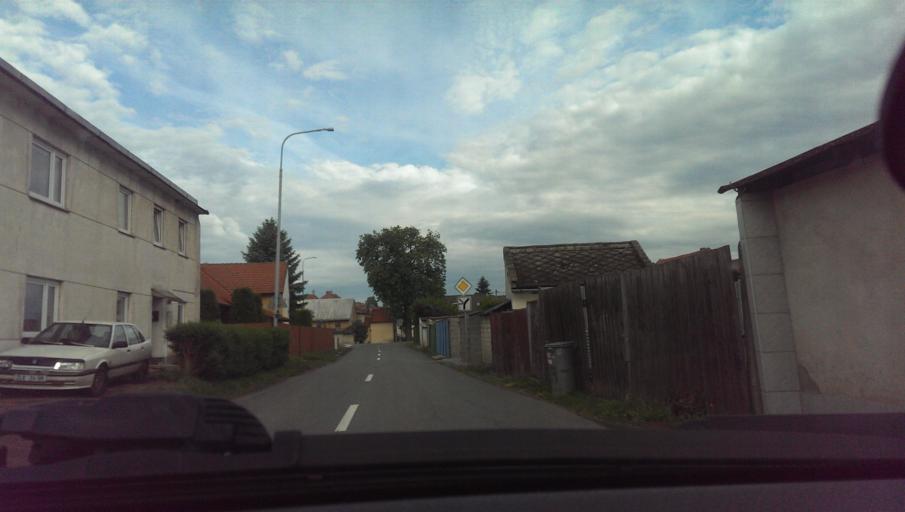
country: CZ
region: Zlin
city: Kvasice
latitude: 49.2374
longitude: 17.4732
